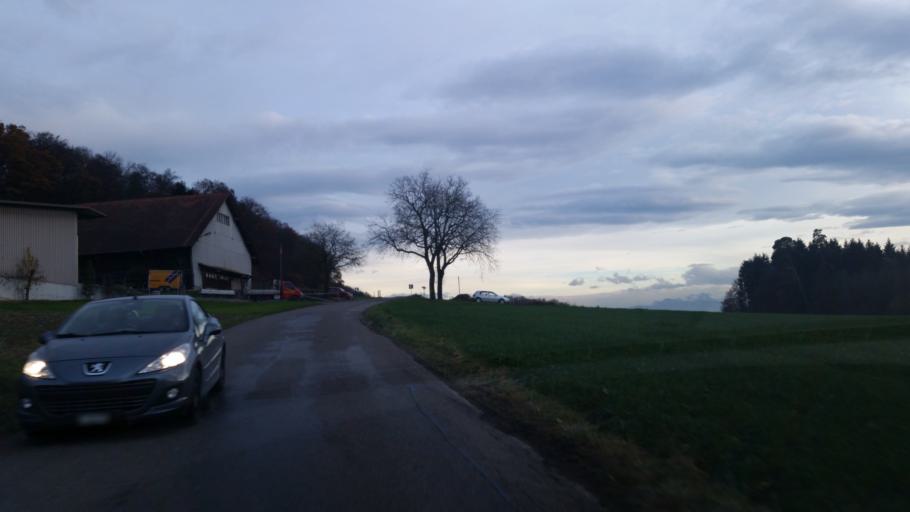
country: CH
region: Aargau
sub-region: Bezirk Baden
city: Kunten
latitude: 47.3829
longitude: 8.3419
